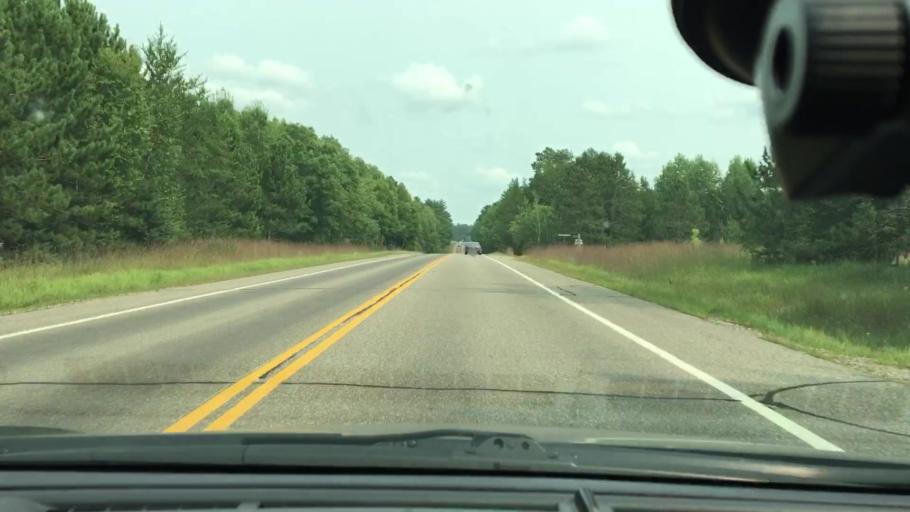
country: US
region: Minnesota
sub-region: Crow Wing County
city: Cross Lake
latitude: 46.7309
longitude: -93.9781
